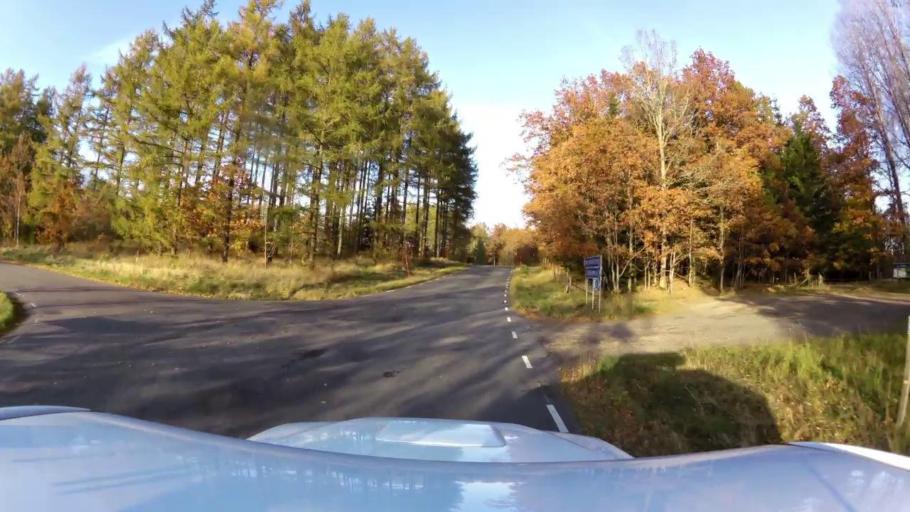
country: SE
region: OEstergoetland
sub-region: Linkopings Kommun
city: Sturefors
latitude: 58.2551
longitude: 15.6623
